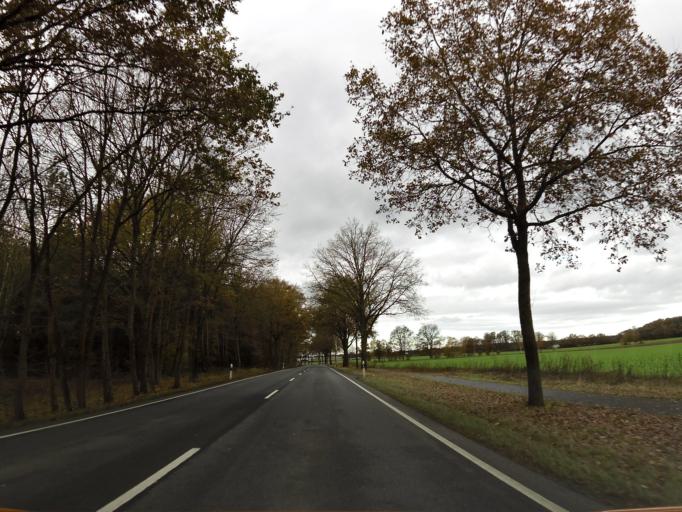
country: DE
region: Lower Saxony
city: Suderburg
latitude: 52.9523
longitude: 10.4967
